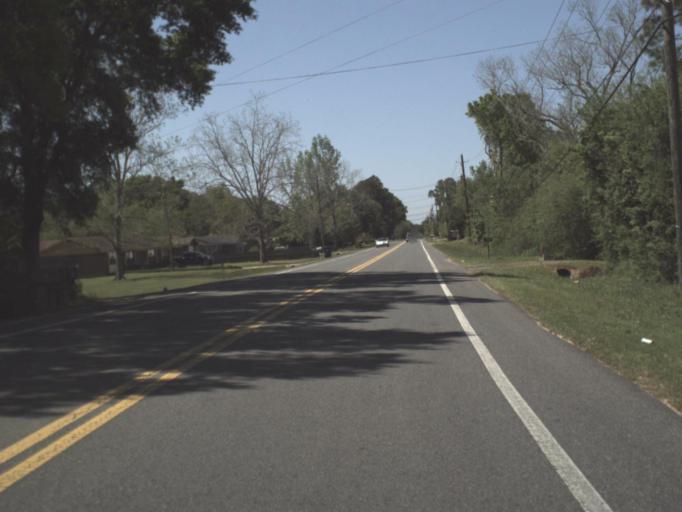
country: US
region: Florida
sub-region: Escambia County
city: Bellview
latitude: 30.5207
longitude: -87.3846
